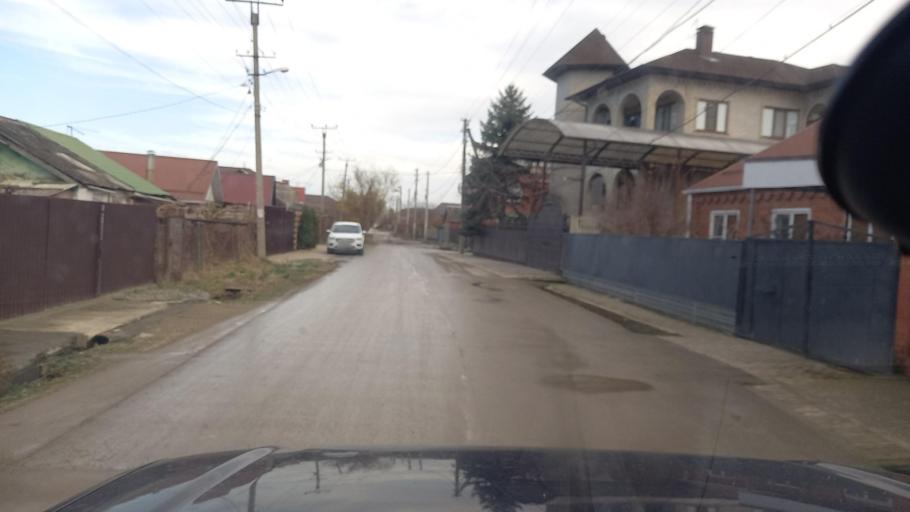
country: RU
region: Adygeya
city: Yablonovskiy
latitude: 44.9834
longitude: 38.9459
